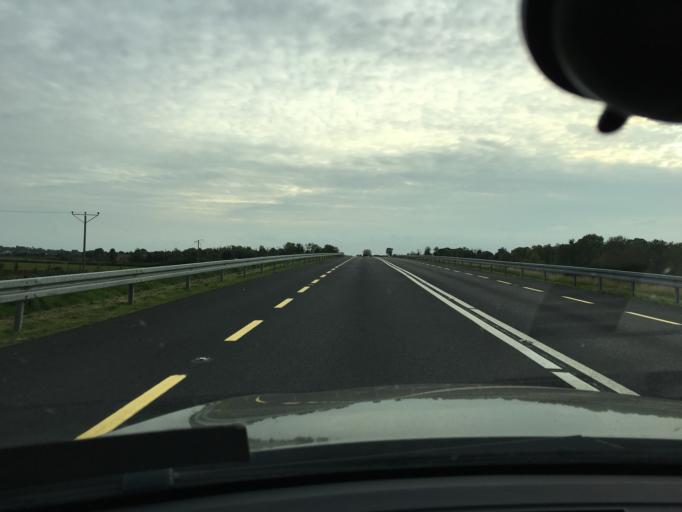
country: IE
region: Leinster
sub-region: An Longfort
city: Longford
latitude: 53.7374
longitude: -7.8163
